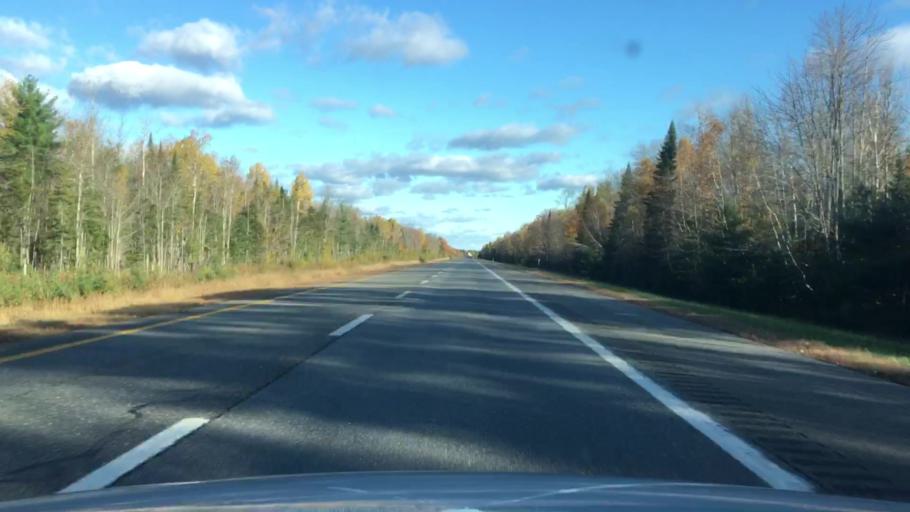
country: US
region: Maine
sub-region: Penobscot County
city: Greenbush
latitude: 45.0797
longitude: -68.6920
